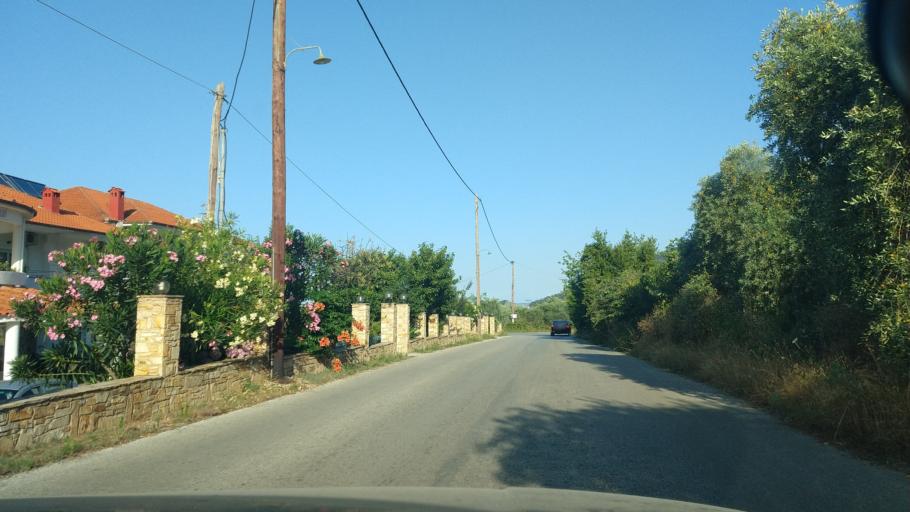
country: GR
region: East Macedonia and Thrace
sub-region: Nomos Kavalas
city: Potamia
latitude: 40.7164
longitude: 24.7441
